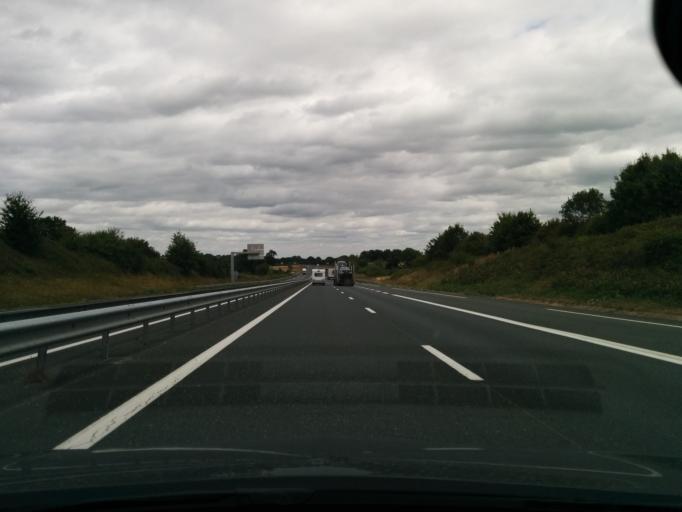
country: FR
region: Centre
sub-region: Departement de l'Indre
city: Le Pechereau
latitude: 46.5102
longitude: 1.5072
